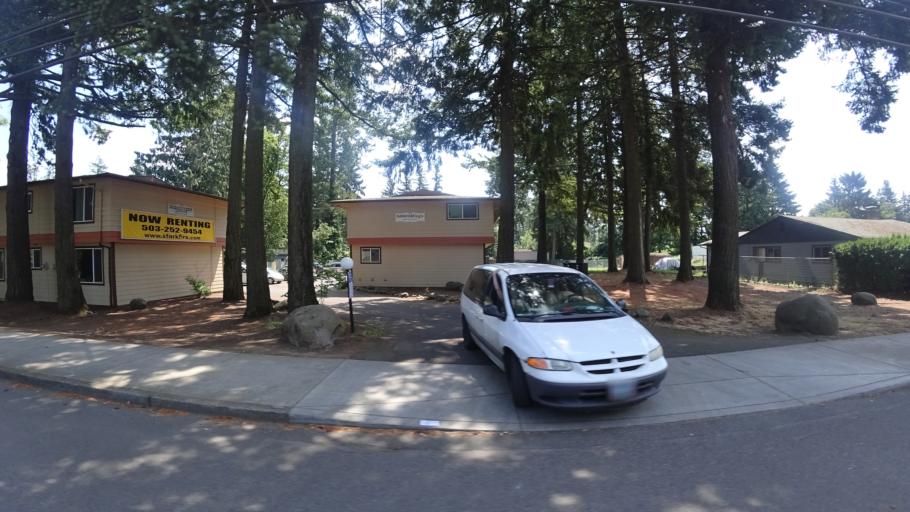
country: US
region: Oregon
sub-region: Multnomah County
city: Fairview
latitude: 45.5264
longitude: -122.5001
